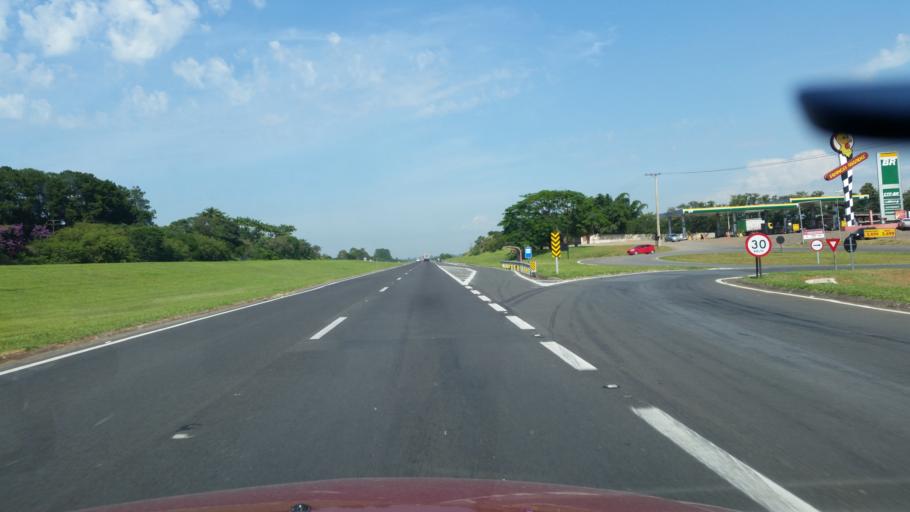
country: BR
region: Sao Paulo
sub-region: Tatui
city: Tatui
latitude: -23.2515
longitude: -47.9671
